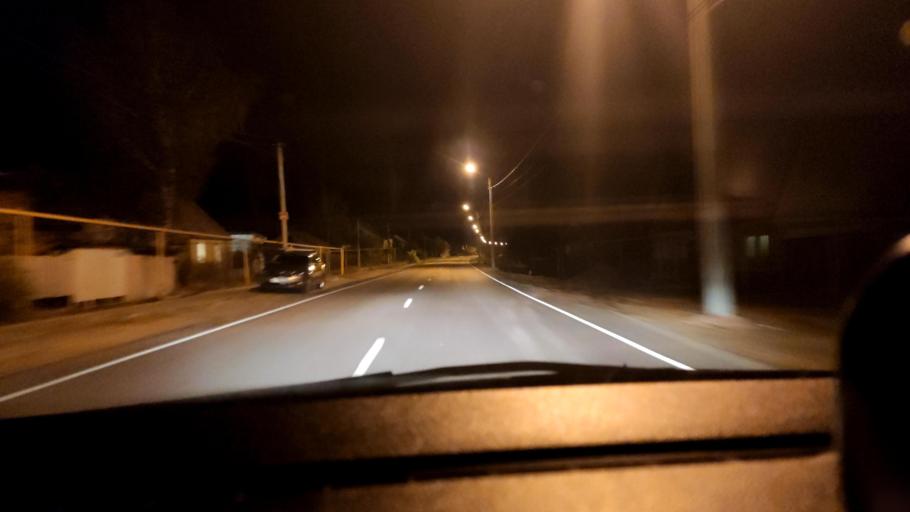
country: RU
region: Voronezj
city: Shilovo
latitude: 51.5632
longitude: 39.0541
